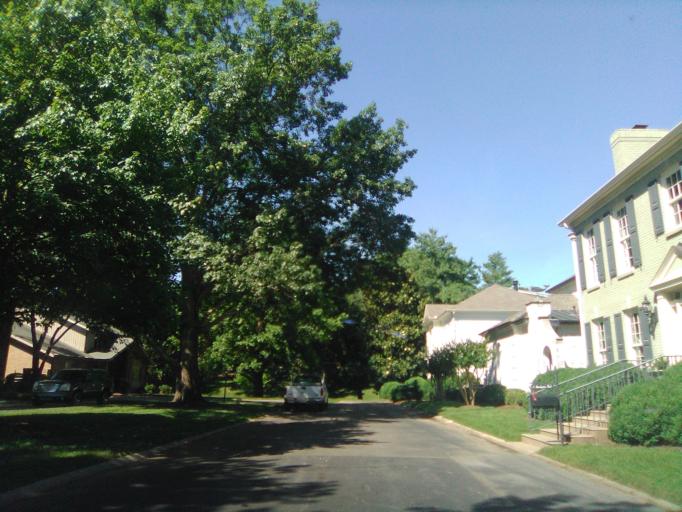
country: US
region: Tennessee
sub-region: Davidson County
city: Belle Meade
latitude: 36.1170
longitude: -86.8418
